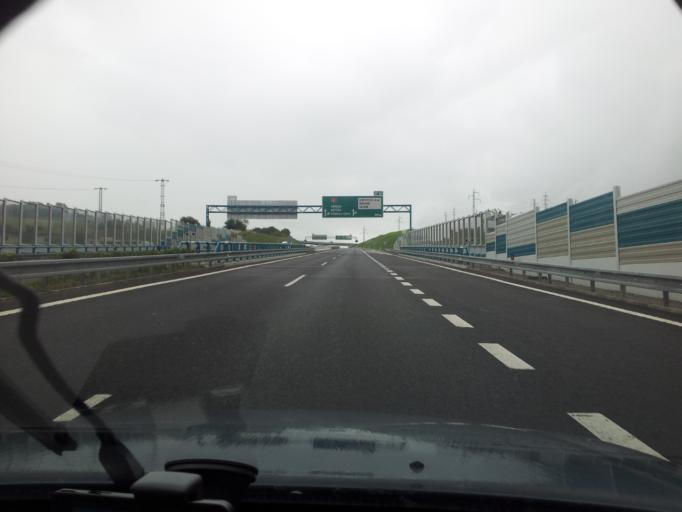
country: SK
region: Banskobystricky
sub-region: Okres Banska Bystrica
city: Banska Bystrica
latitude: 48.7496
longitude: 19.1441
